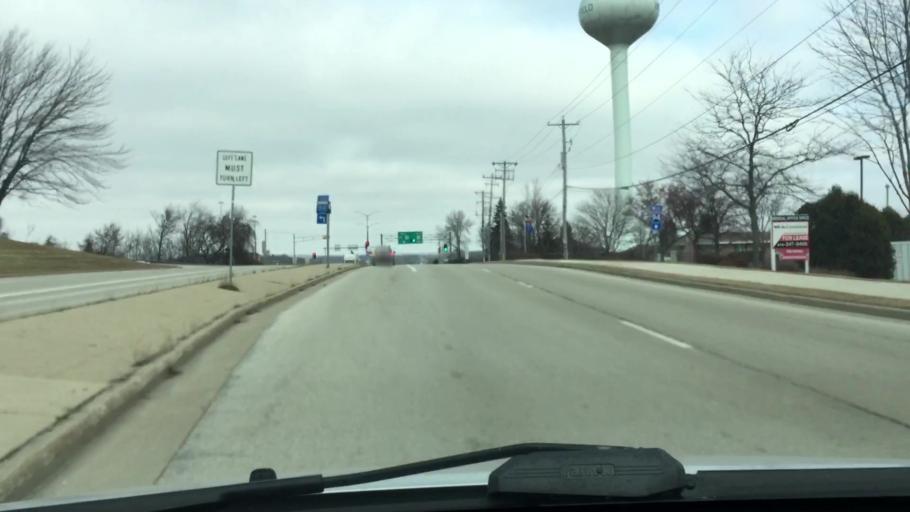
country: US
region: Wisconsin
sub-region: Waukesha County
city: Brookfield
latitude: 43.0306
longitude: -88.1668
